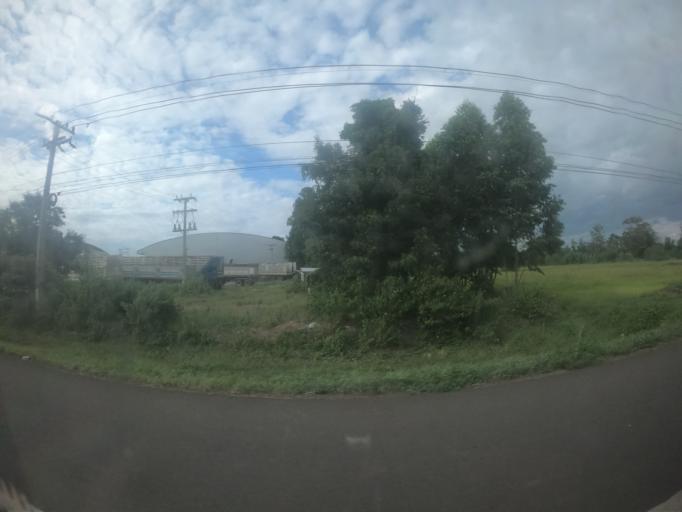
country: TH
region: Surin
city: Prasat
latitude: 14.5943
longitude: 103.4448
